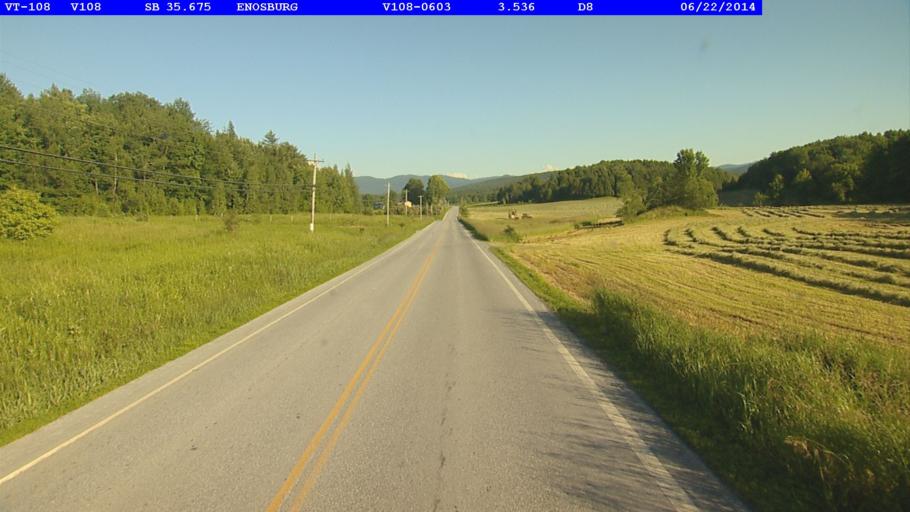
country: US
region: Vermont
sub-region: Franklin County
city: Enosburg Falls
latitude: 44.8866
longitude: -72.8023
